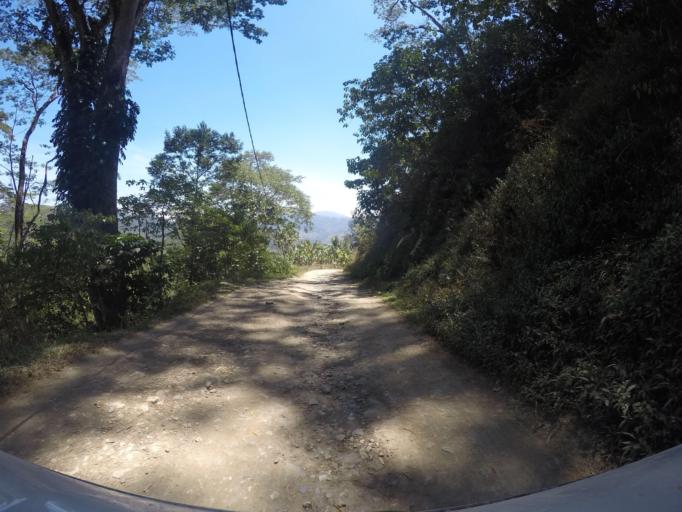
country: TL
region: Ermera
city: Gleno
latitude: -8.7406
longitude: 125.4067
